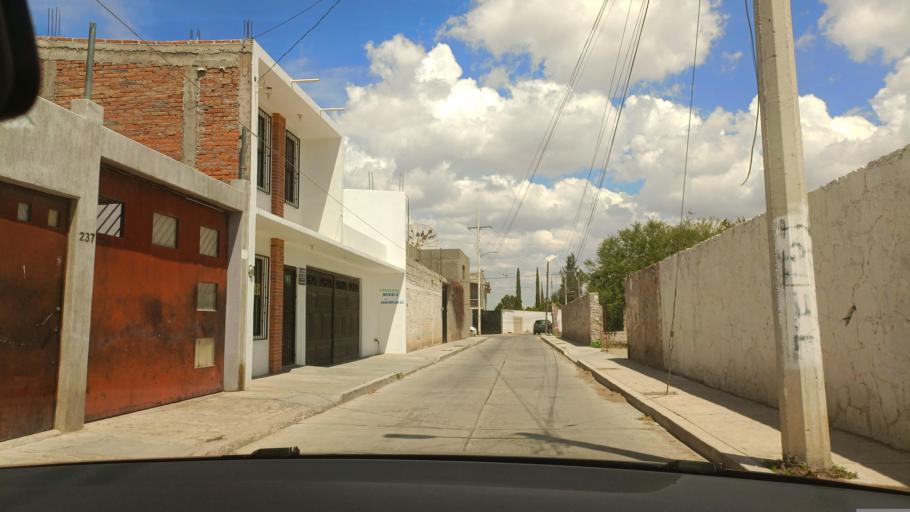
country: MX
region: Guanajuato
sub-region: San Luis de la Paz
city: San Luis de la Paz
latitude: 21.3033
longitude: -100.5189
